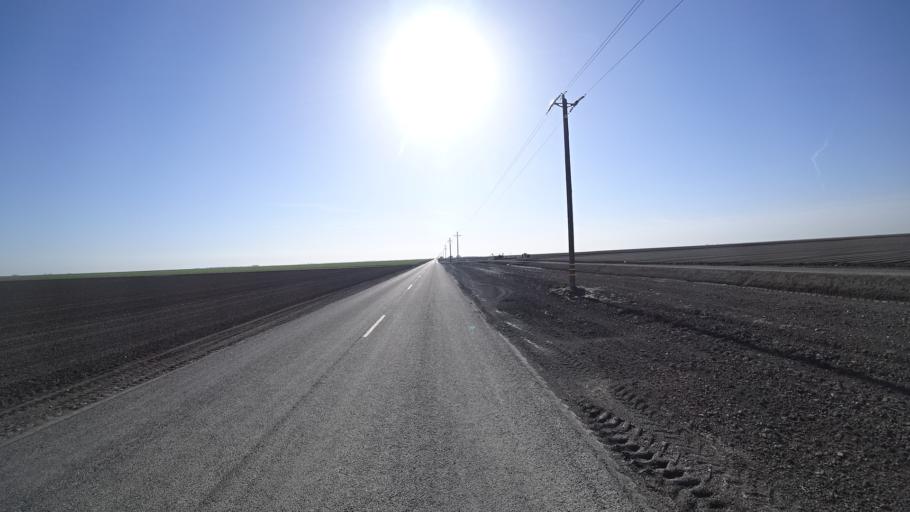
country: US
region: California
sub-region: Kings County
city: Corcoran
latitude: 36.0797
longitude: -119.6997
